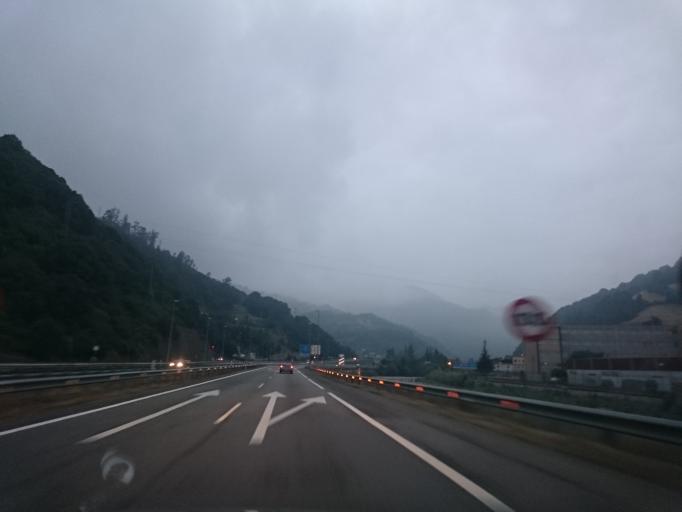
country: ES
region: Asturias
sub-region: Province of Asturias
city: Mieres
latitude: 43.2061
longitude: -5.7876
